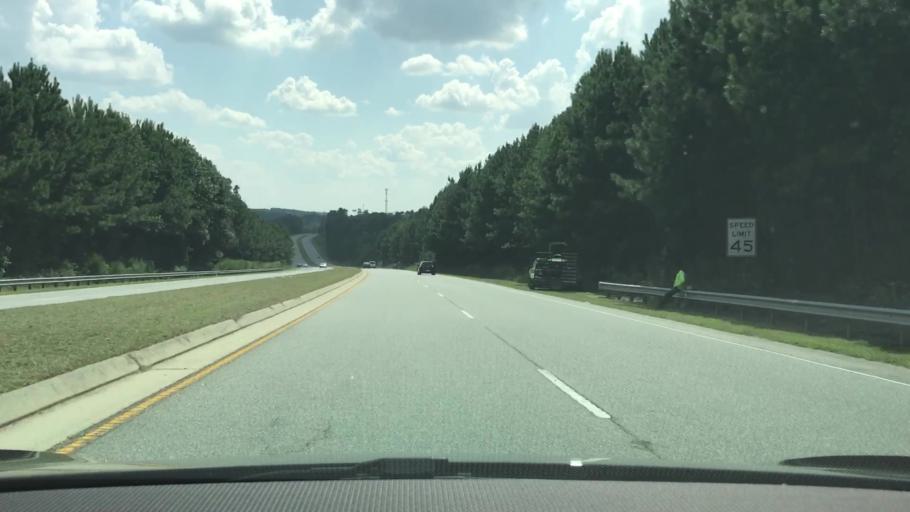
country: US
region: Georgia
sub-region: Gwinnett County
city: Suwanee
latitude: 34.0576
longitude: -84.0236
